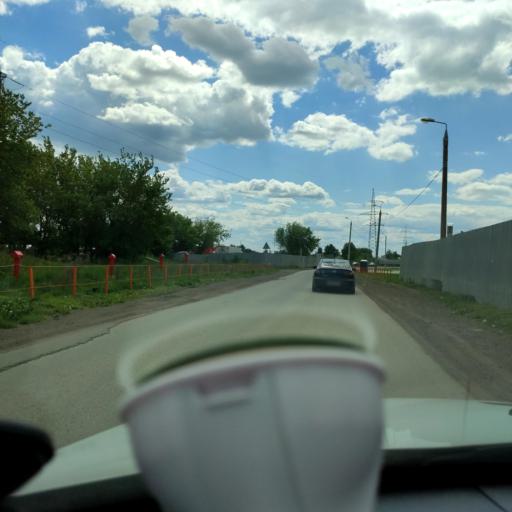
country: RU
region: Samara
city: Petra-Dubrava
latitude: 53.2649
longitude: 50.3173
